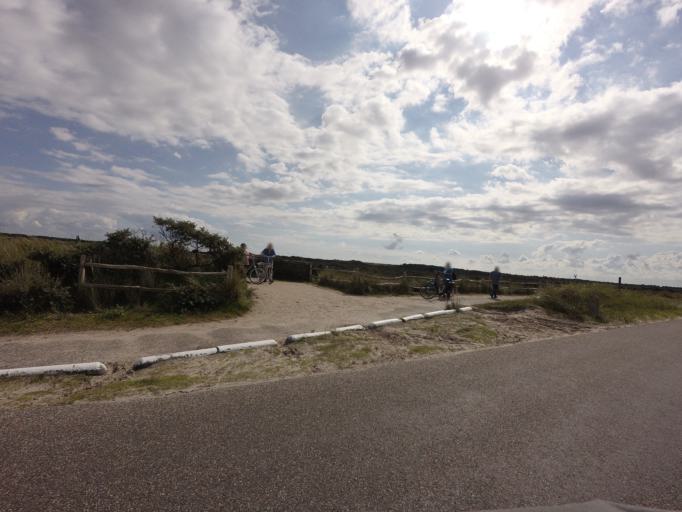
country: NL
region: Friesland
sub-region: Gemeente Terschelling
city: West-Terschelling
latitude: 53.3973
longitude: 5.2549
